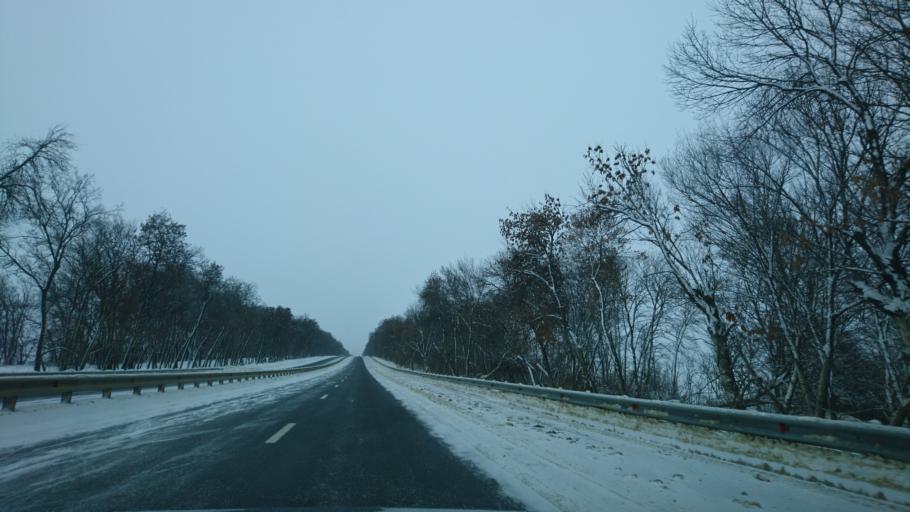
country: RU
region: Belgorod
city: Bessonovka
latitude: 50.3662
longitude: 36.3175
